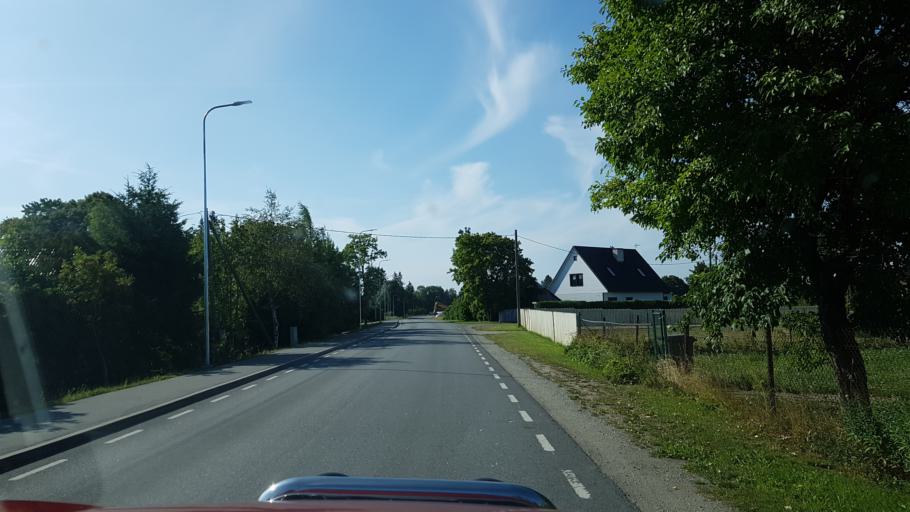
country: EE
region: Harju
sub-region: Joelaehtme vald
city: Loo
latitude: 59.3970
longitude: 24.9334
